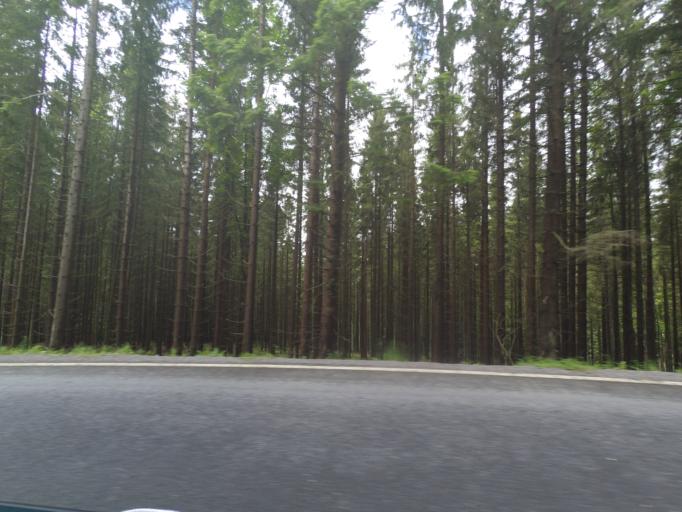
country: CZ
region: Plzensky
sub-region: Okres Klatovy
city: Zelezna Ruda
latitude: 49.1820
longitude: 13.2358
